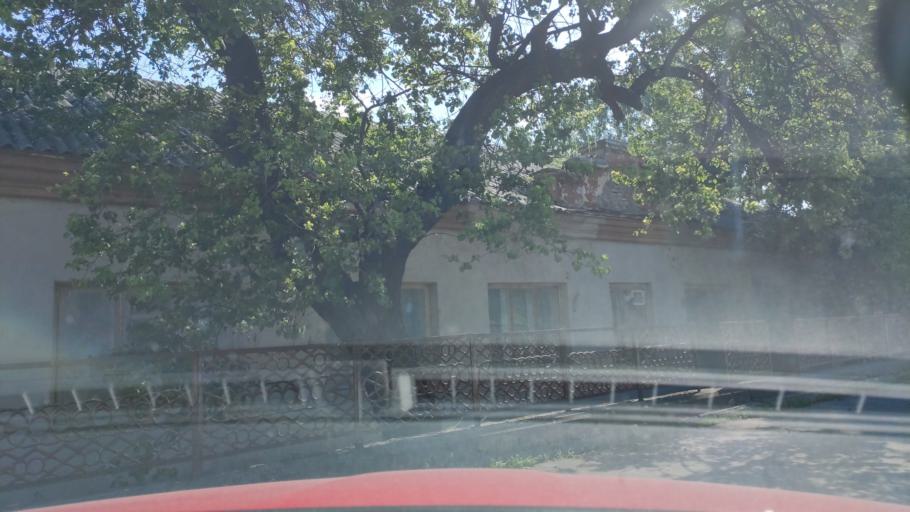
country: MD
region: Raionul Soroca
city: Soroca
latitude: 48.1717
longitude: 28.3161
